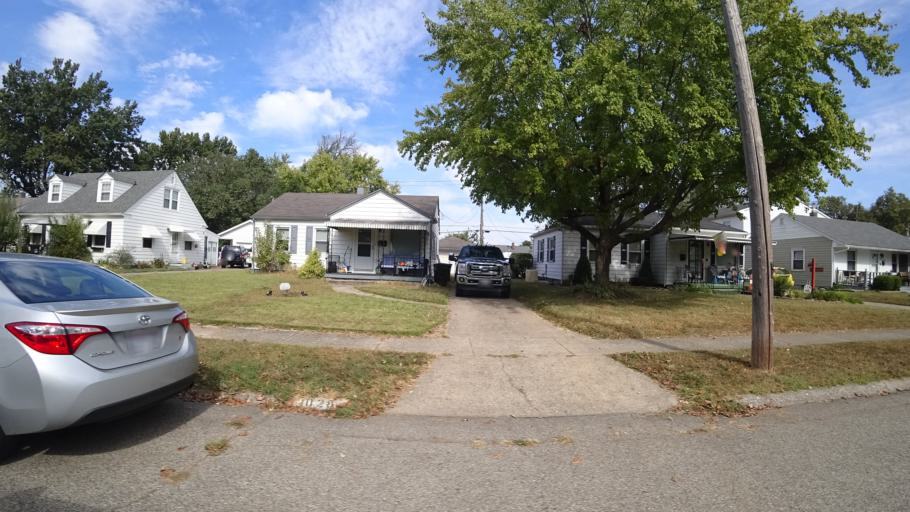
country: US
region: Ohio
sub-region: Butler County
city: Fairfield
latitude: 39.3609
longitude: -84.5503
